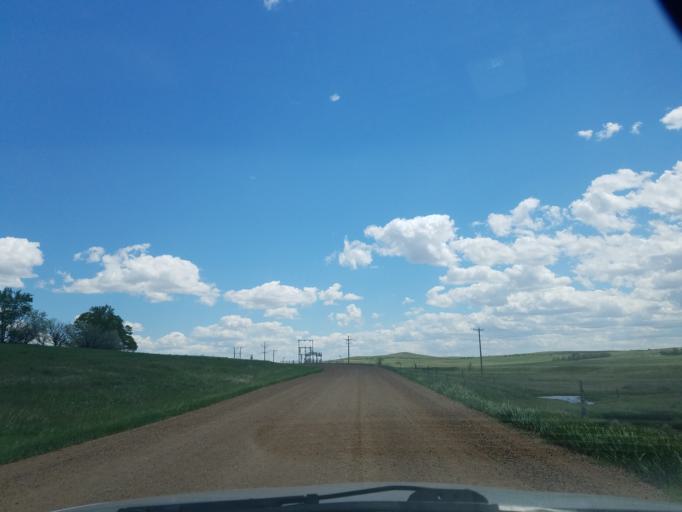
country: US
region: North Dakota
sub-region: Williams County
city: Williston
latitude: 47.8343
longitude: -103.6341
